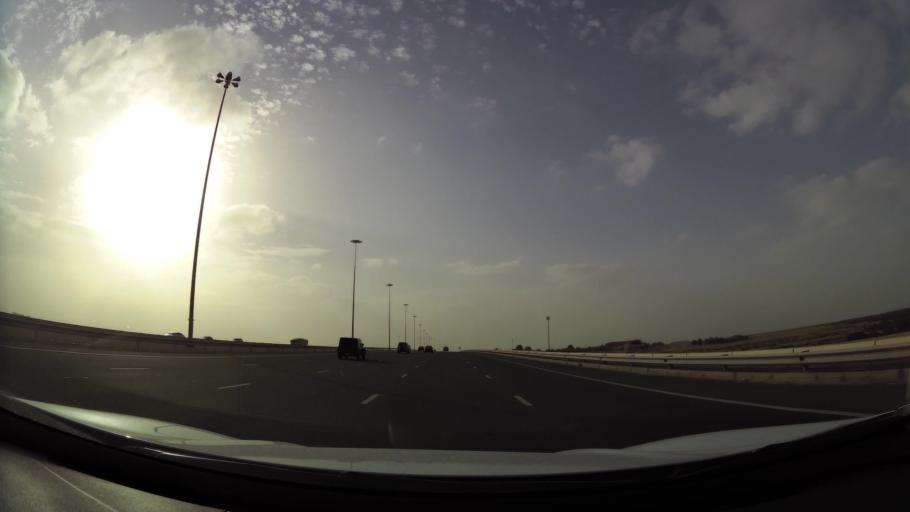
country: AE
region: Abu Dhabi
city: Abu Dhabi
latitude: 24.5268
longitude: 54.5017
